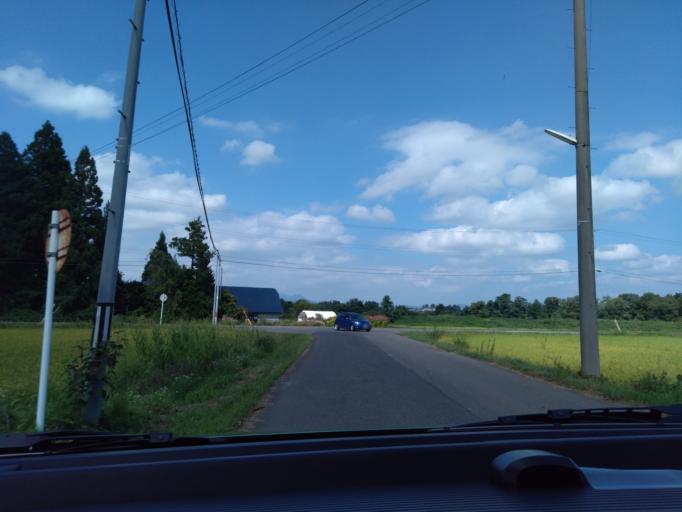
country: JP
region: Iwate
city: Shizukuishi
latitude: 39.6829
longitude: 140.9599
